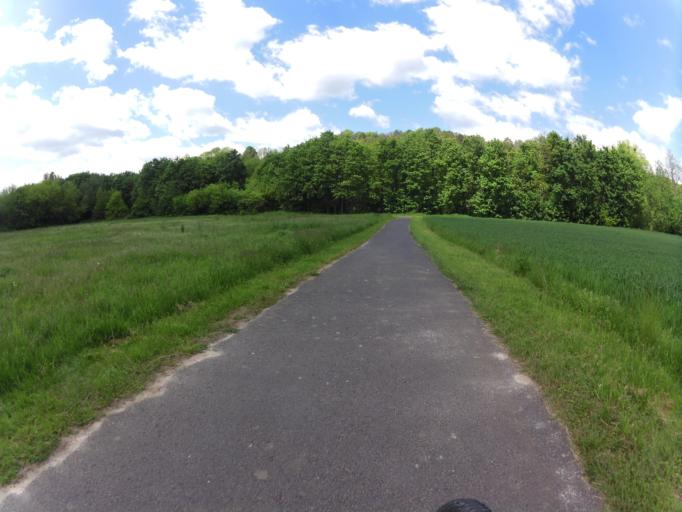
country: DE
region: Thuringia
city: Mihla
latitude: 51.0863
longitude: 10.3218
